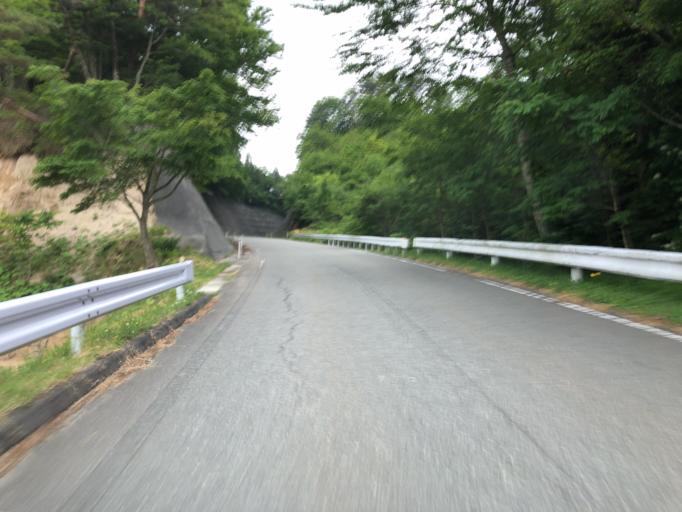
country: JP
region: Fukushima
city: Funehikimachi-funehiki
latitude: 37.3807
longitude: 140.7533
